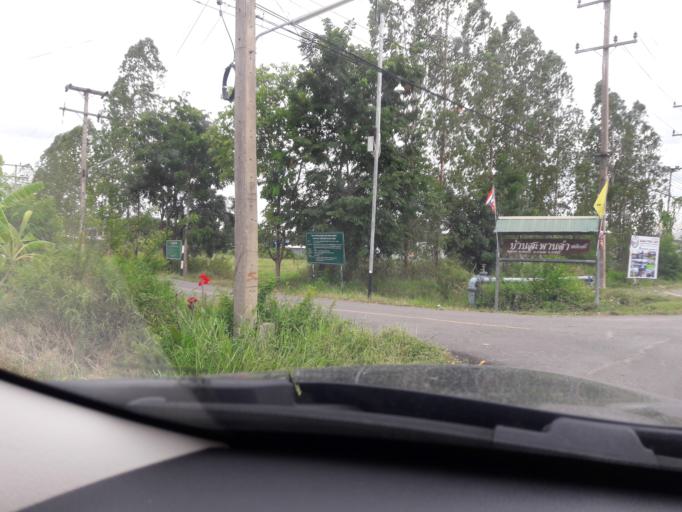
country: TH
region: Ratchaburi
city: Bang Phae
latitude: 13.6288
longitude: 99.9487
